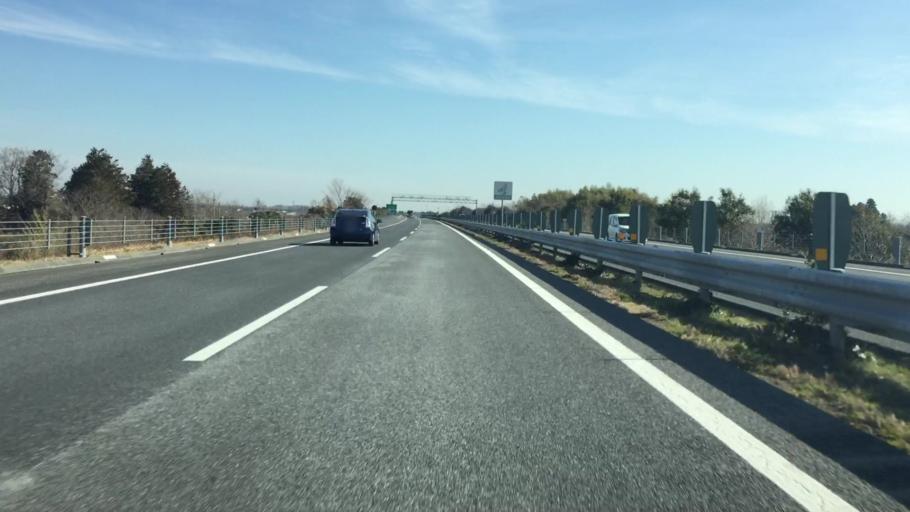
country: JP
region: Ibaraki
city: Mito-shi
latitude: 36.3213
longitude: 140.4764
